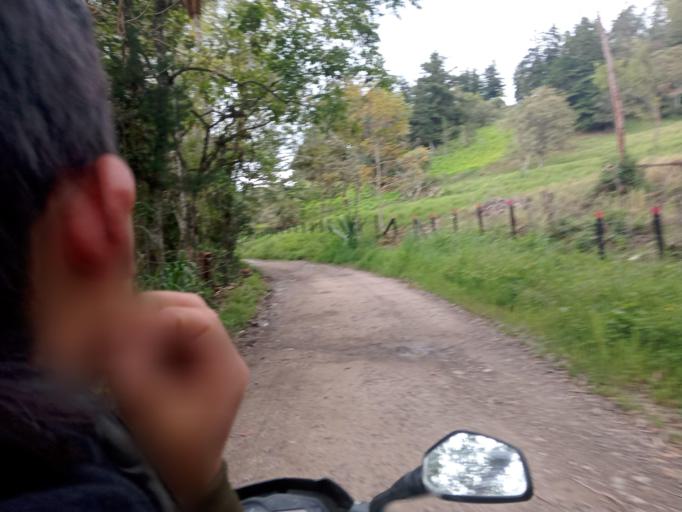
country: CO
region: Cundinamarca
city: Tenza
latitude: 5.1018
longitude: -73.4263
